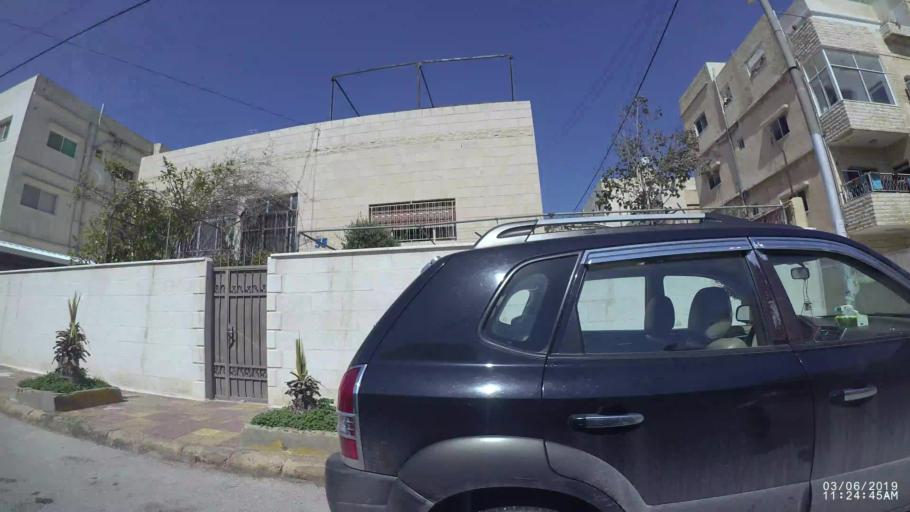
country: JO
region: Amman
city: Amman
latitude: 31.9771
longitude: 35.9932
